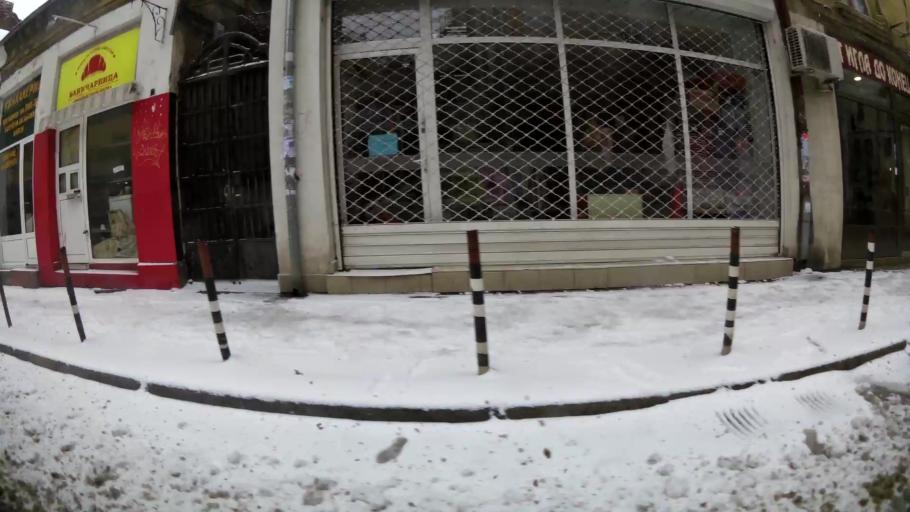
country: BG
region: Sofia-Capital
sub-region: Stolichna Obshtina
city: Sofia
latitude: 42.7001
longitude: 23.3164
